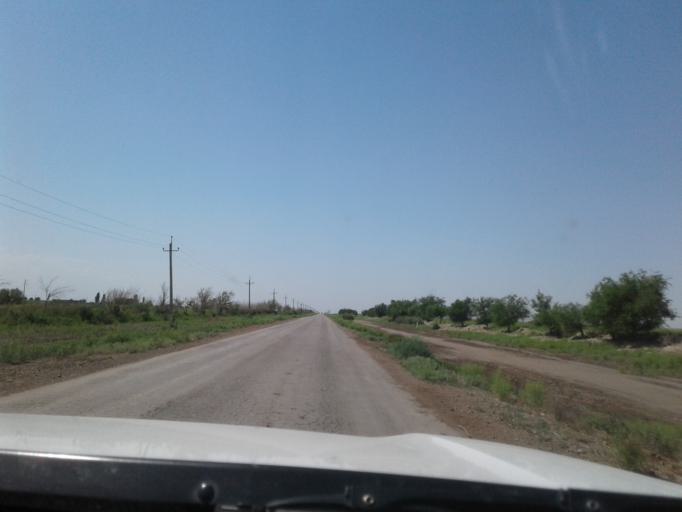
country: TM
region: Dasoguz
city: Koeneuergench
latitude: 41.8544
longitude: 58.7052
